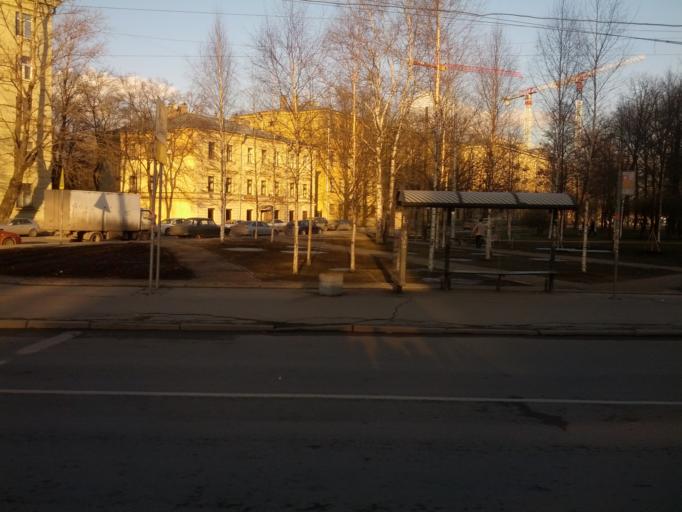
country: RU
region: St.-Petersburg
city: Centralniy
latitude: 59.9336
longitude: 30.4076
